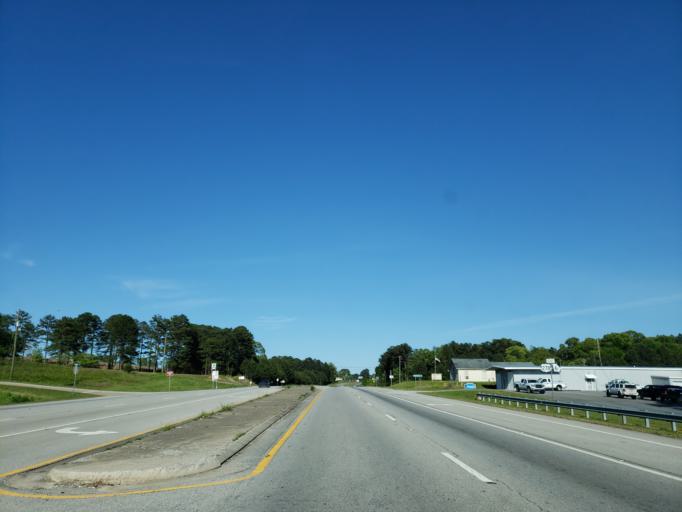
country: US
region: Georgia
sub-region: Polk County
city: Cedartown
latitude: 34.0171
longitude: -85.2181
